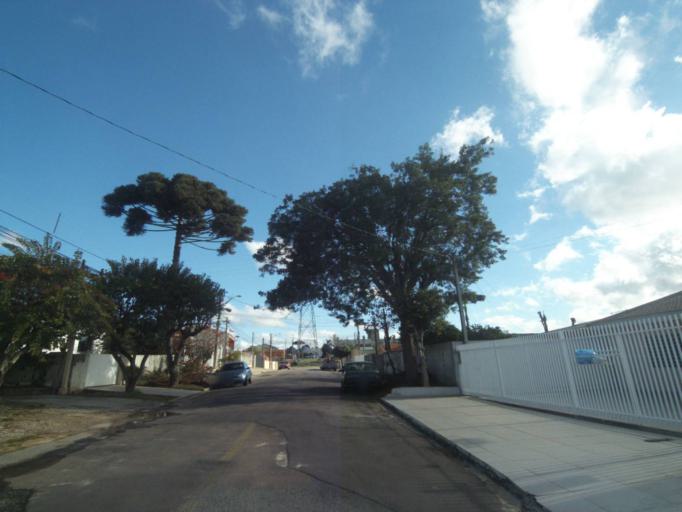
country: BR
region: Parana
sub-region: Sao Jose Dos Pinhais
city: Sao Jose dos Pinhais
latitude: -25.5283
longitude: -49.2891
